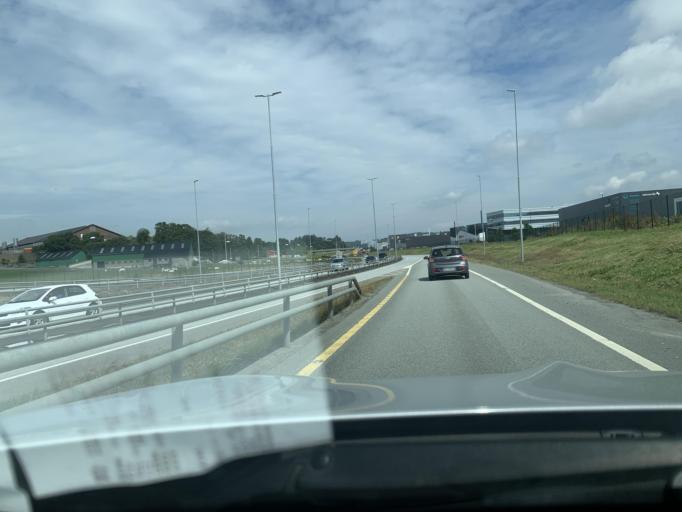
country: NO
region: Rogaland
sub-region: Sola
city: Sola
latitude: 58.8969
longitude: 5.6785
